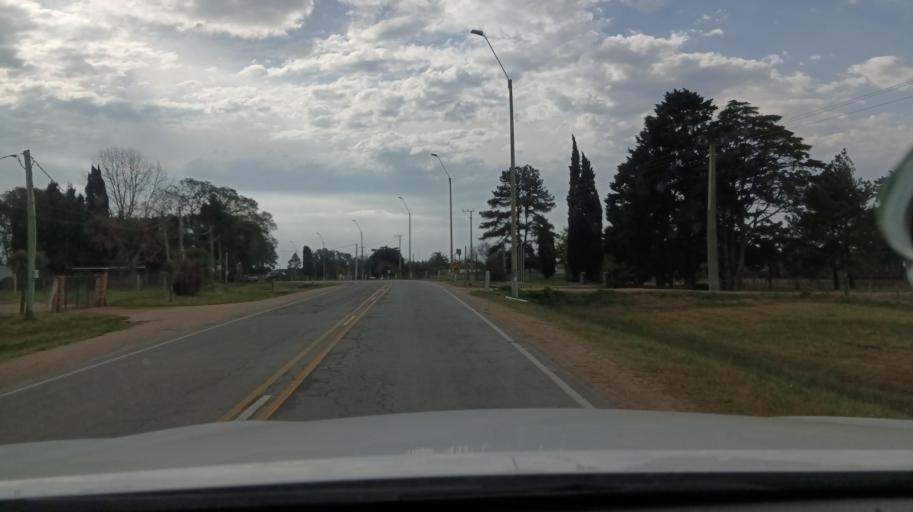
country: UY
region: Canelones
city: Toledo
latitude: -34.7039
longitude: -56.1047
